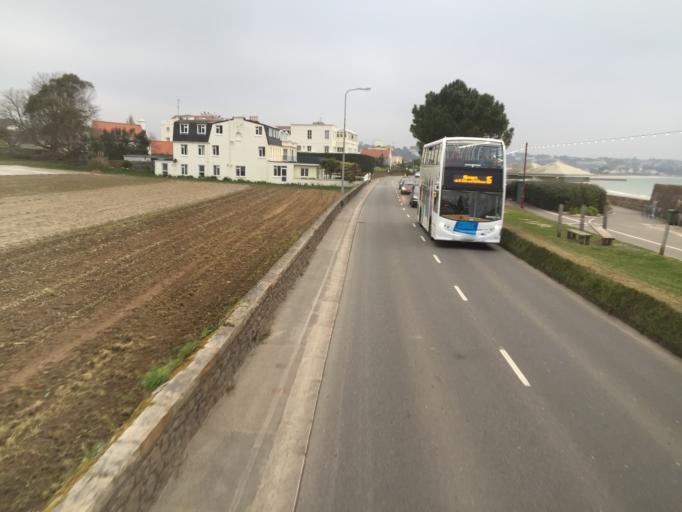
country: JE
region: St Helier
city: Saint Helier
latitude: 49.1936
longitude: -2.1651
